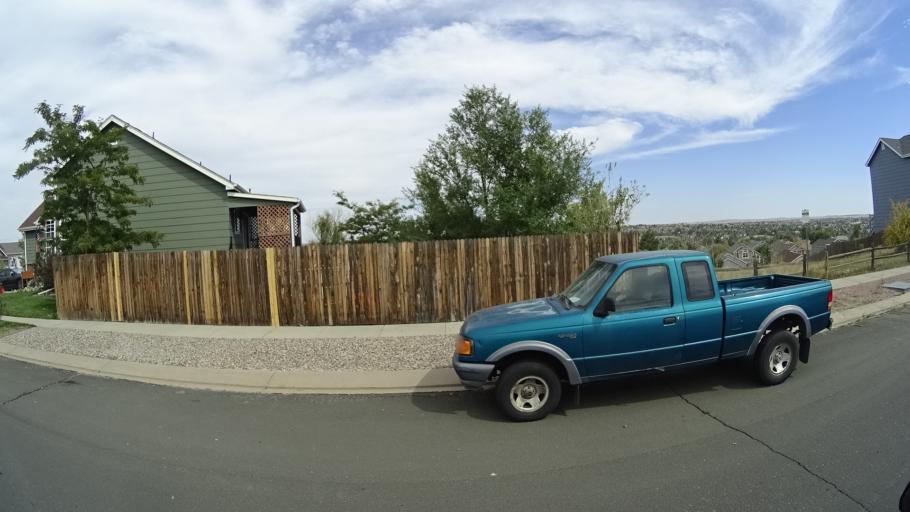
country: US
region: Colorado
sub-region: El Paso County
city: Cimarron Hills
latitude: 38.9035
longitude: -104.7179
